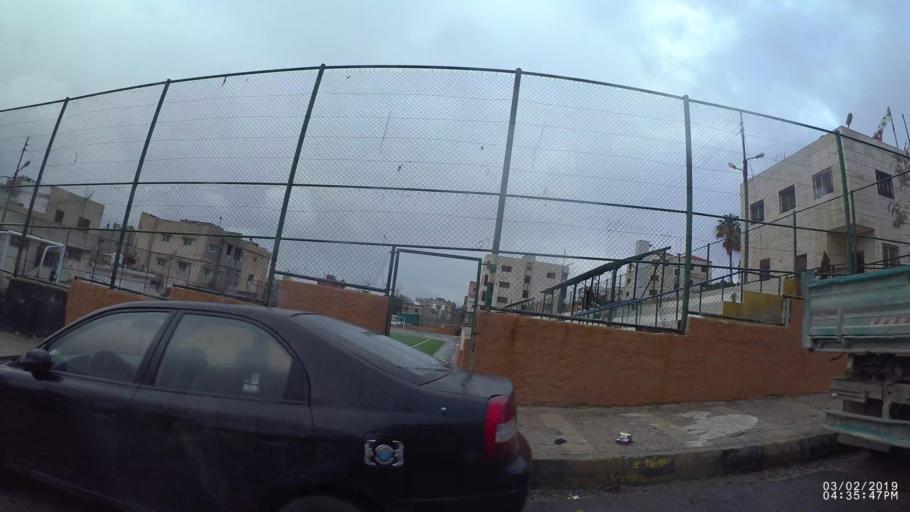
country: JO
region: Amman
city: Amman
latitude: 31.9668
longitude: 35.9237
